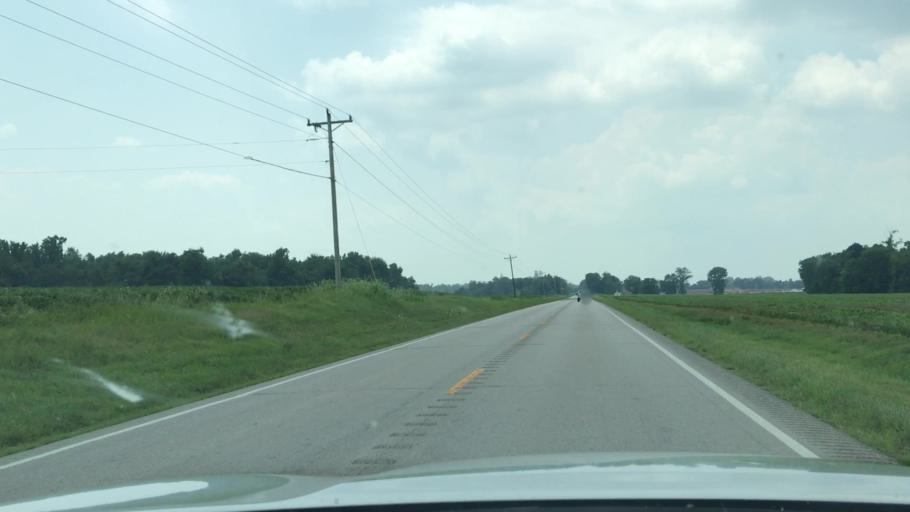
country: US
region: Kentucky
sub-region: Todd County
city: Guthrie
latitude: 36.6668
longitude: -87.1644
